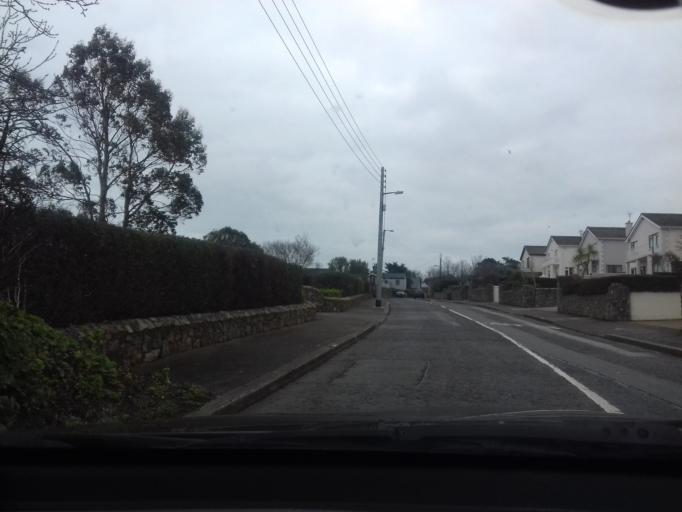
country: IE
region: Leinster
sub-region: Fingal County
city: Howth
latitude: 53.3810
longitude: -6.0666
